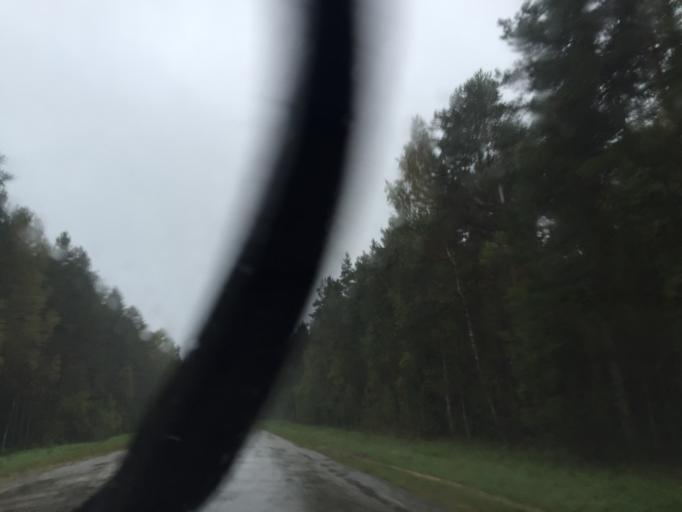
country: LV
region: Ropazu
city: Ropazi
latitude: 57.0033
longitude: 24.6719
